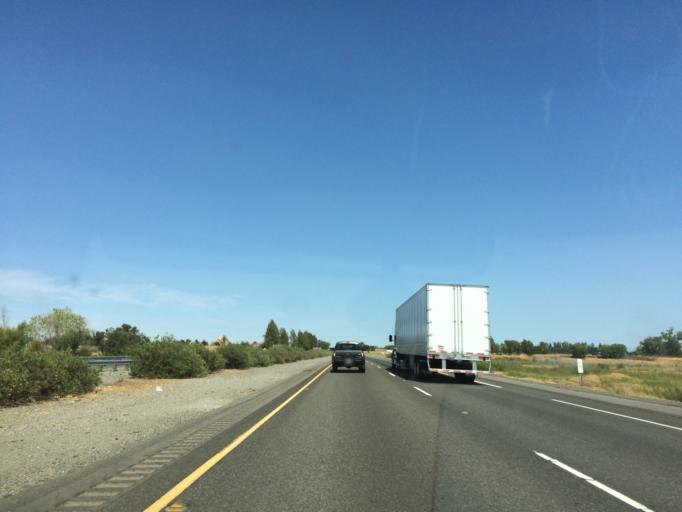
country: US
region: California
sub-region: Glenn County
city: Orland
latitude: 39.7726
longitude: -122.2047
